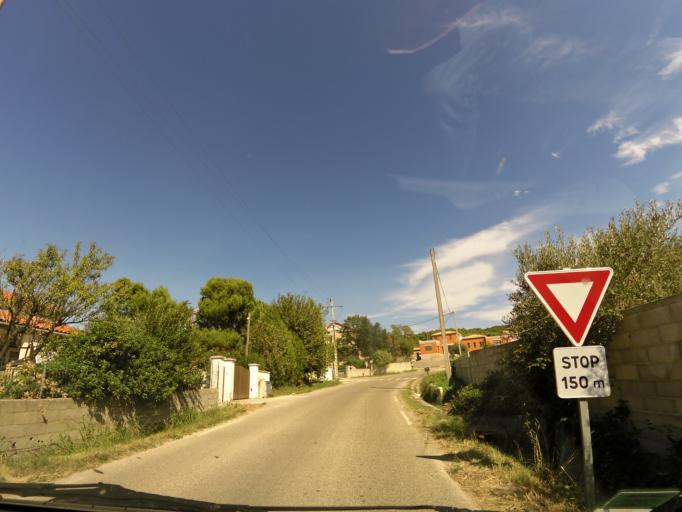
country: FR
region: Languedoc-Roussillon
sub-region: Departement du Gard
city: Nages-et-Solorgues
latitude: 43.7875
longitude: 4.2317
